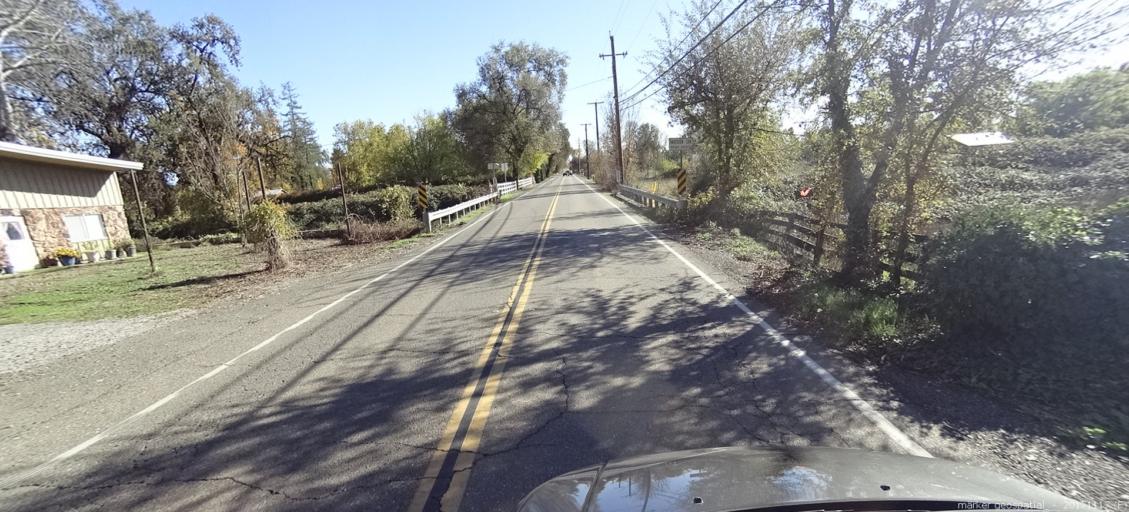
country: US
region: California
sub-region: Shasta County
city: Anderson
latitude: 40.4438
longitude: -122.2504
